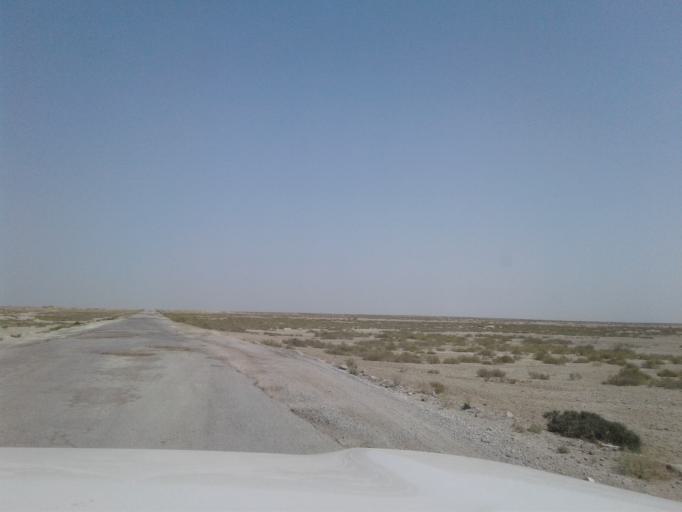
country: IR
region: Golestan
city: Gomishan
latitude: 37.9342
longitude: 53.8463
